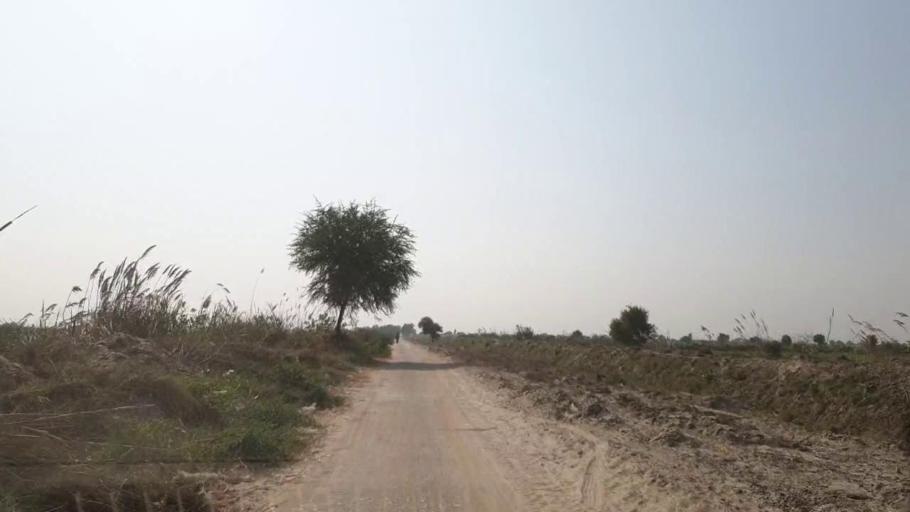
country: PK
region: Sindh
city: Bulri
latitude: 24.9705
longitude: 68.3969
